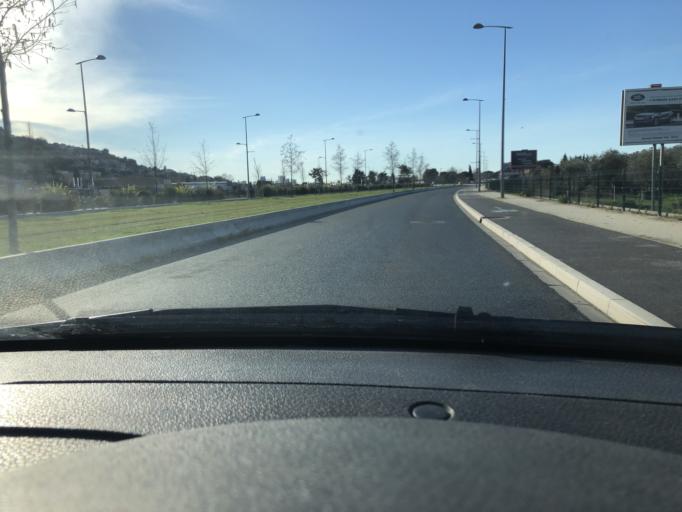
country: FR
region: Provence-Alpes-Cote d'Azur
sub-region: Departement des Alpes-Maritimes
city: Saint-Laurent-du-Var
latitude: 43.7023
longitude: 7.1968
